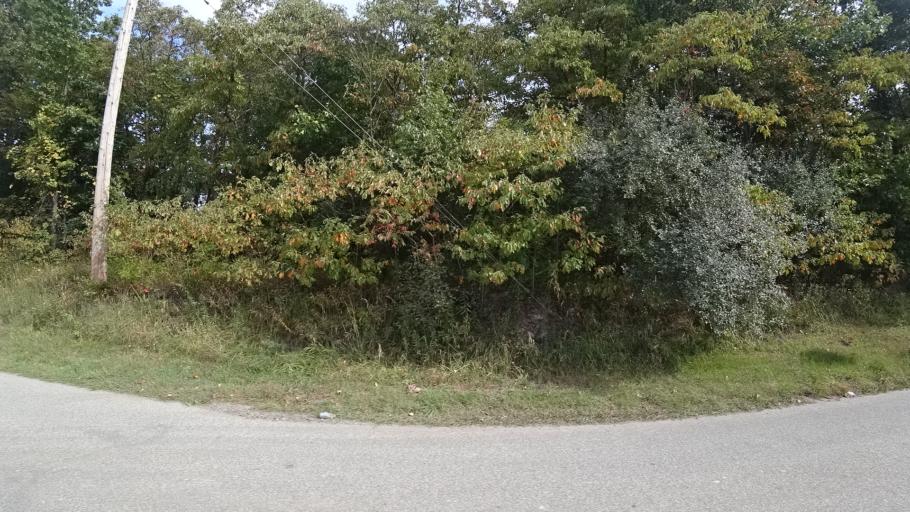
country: US
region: Indiana
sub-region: LaPorte County
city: Trail Creek
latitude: 41.7120
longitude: -86.8553
